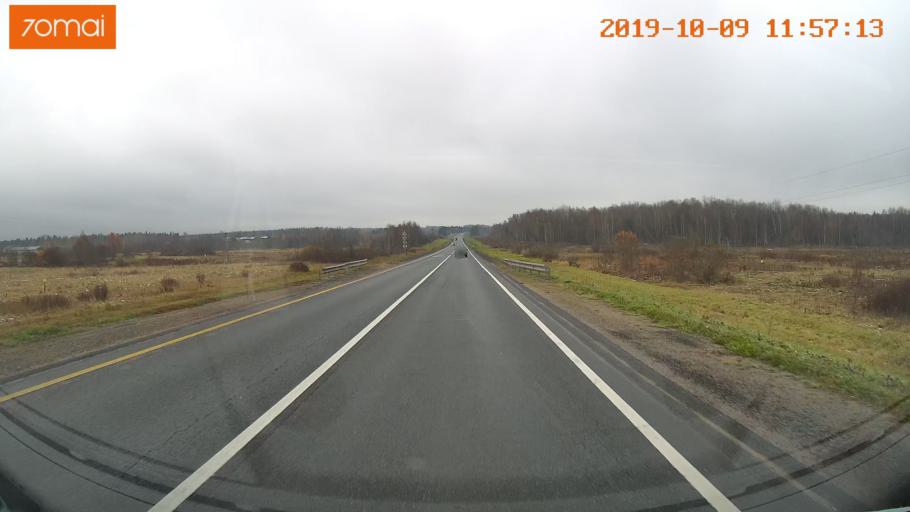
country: RU
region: Vologda
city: Gryazovets
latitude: 58.7351
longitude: 40.2914
